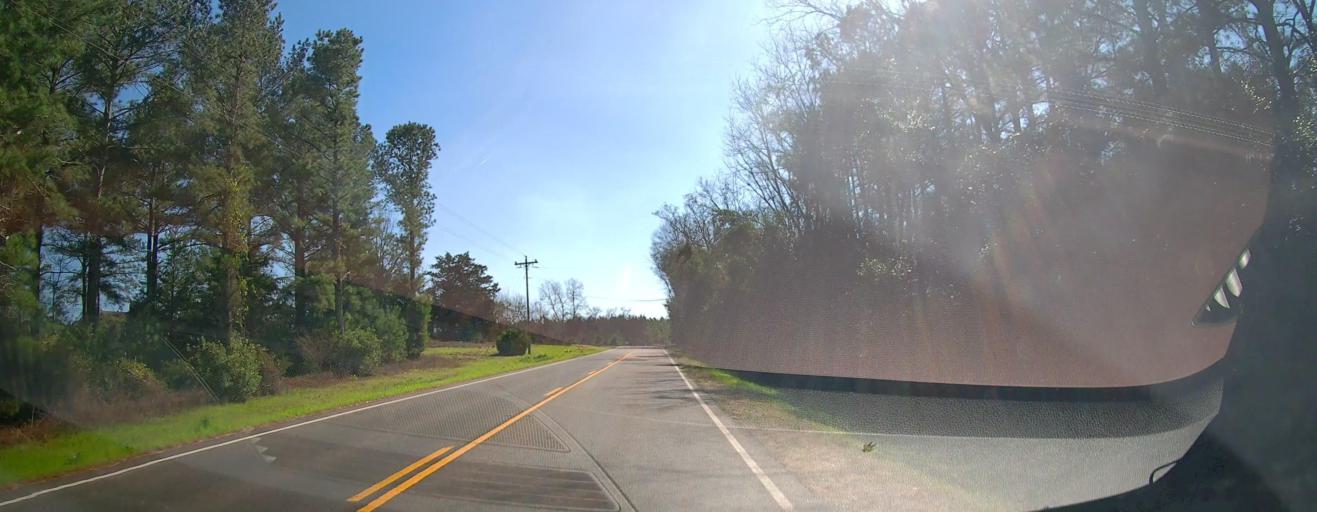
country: US
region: Georgia
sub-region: Macon County
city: Montezuma
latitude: 32.3615
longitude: -84.0143
